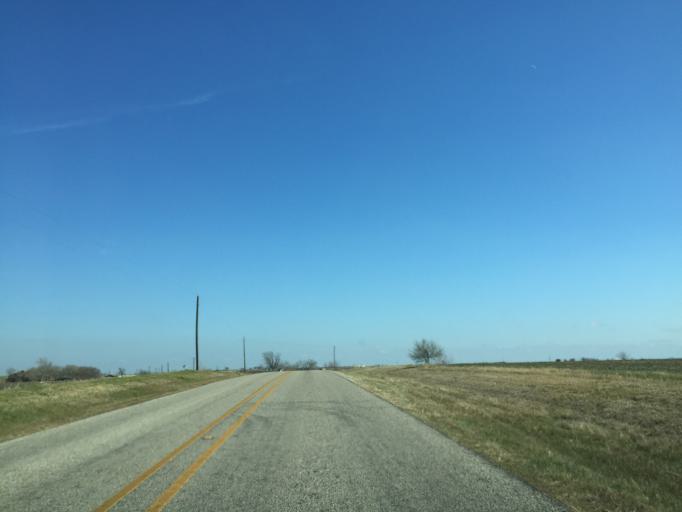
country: US
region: Texas
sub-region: Williamson County
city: Granger
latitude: 30.7470
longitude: -97.5602
